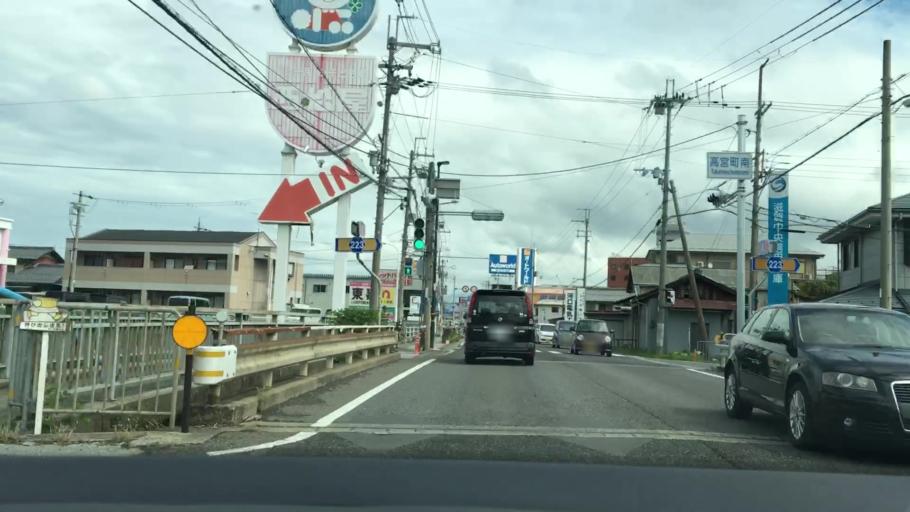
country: JP
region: Shiga Prefecture
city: Hikone
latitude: 35.2377
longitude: 136.2535
